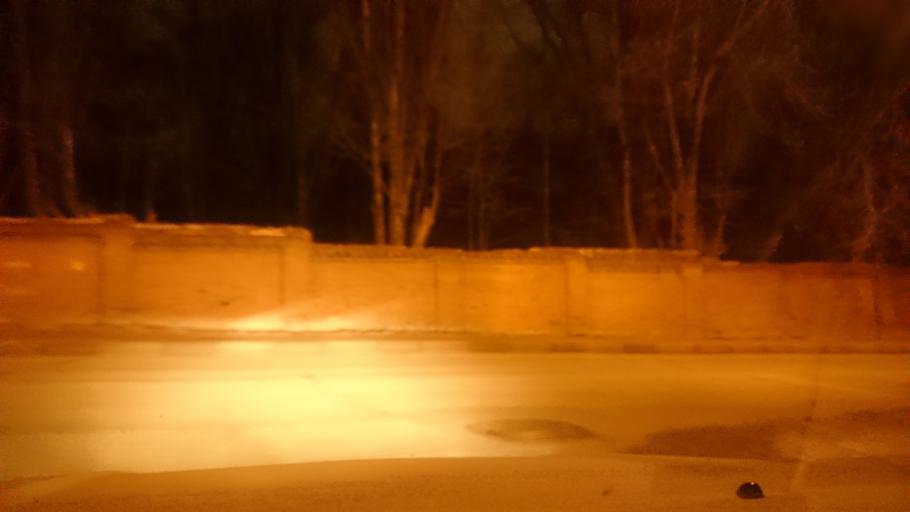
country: RU
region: Tula
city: Tula
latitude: 54.1783
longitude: 37.6154
